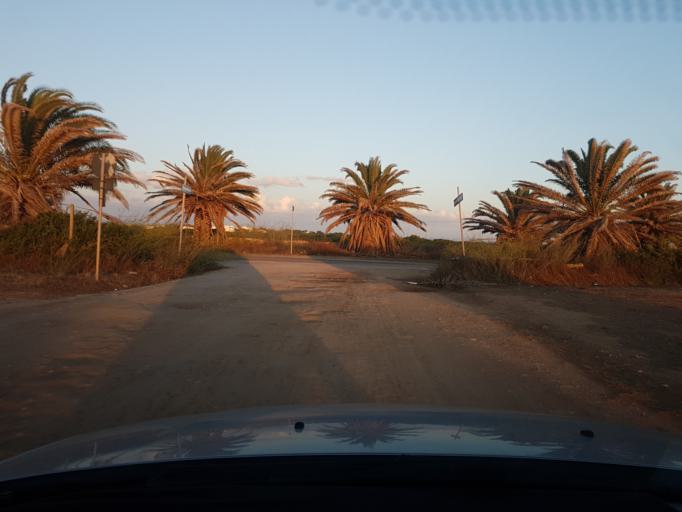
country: IT
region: Sardinia
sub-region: Provincia di Oristano
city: Riola Sardo
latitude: 40.0426
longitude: 8.4022
